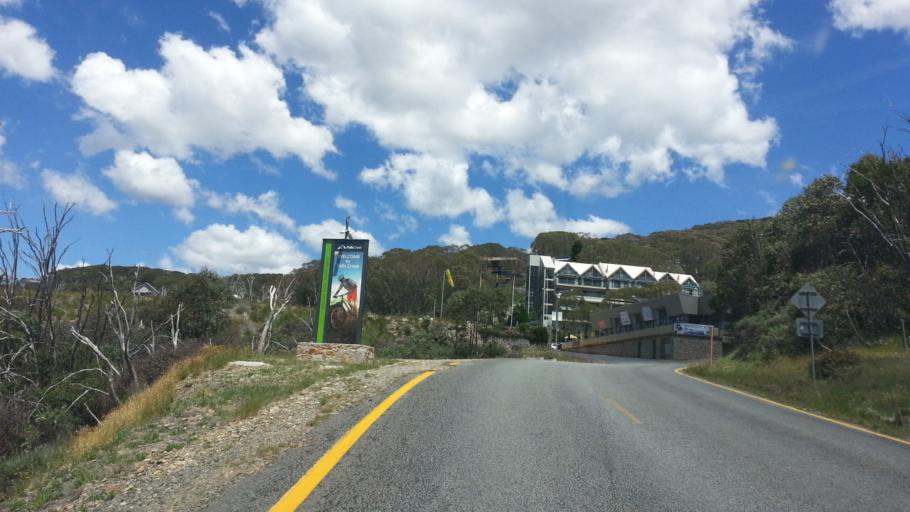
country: AU
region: Victoria
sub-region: Alpine
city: Mount Beauty
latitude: -36.8607
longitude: 147.2764
